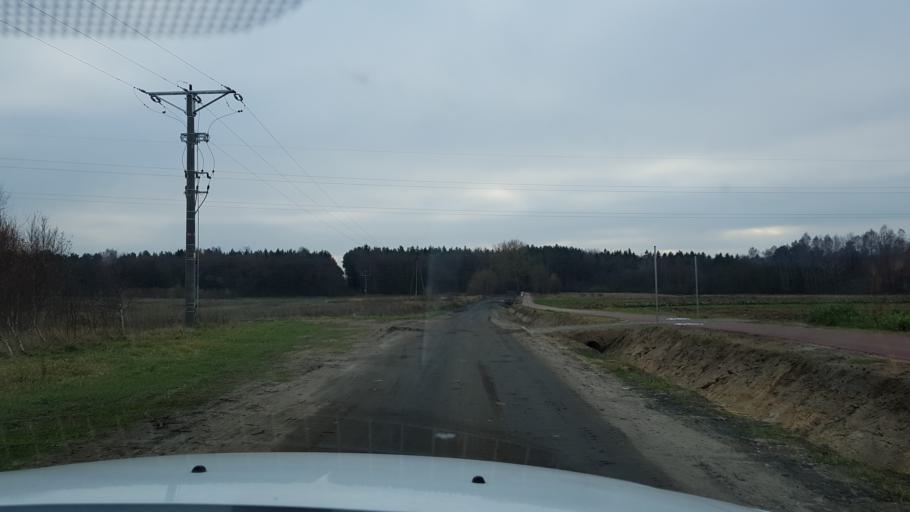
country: PL
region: West Pomeranian Voivodeship
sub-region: Powiat kolobrzeski
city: Grzybowo
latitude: 54.1378
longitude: 15.5144
